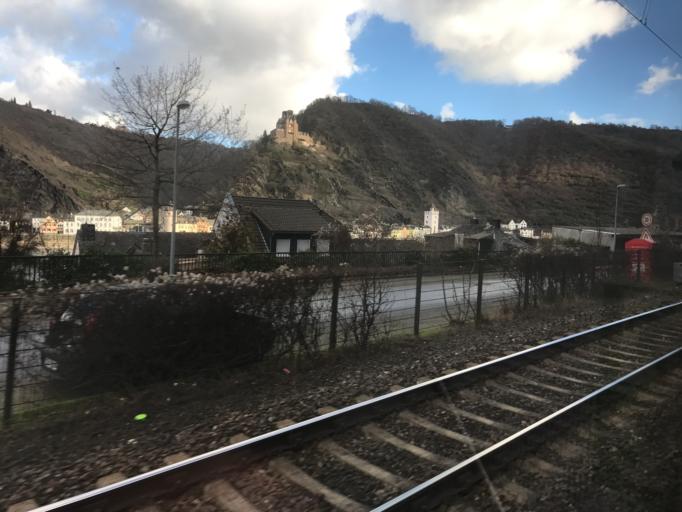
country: DE
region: Rheinland-Pfalz
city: Sankt Goar
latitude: 50.1495
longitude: 7.7171
